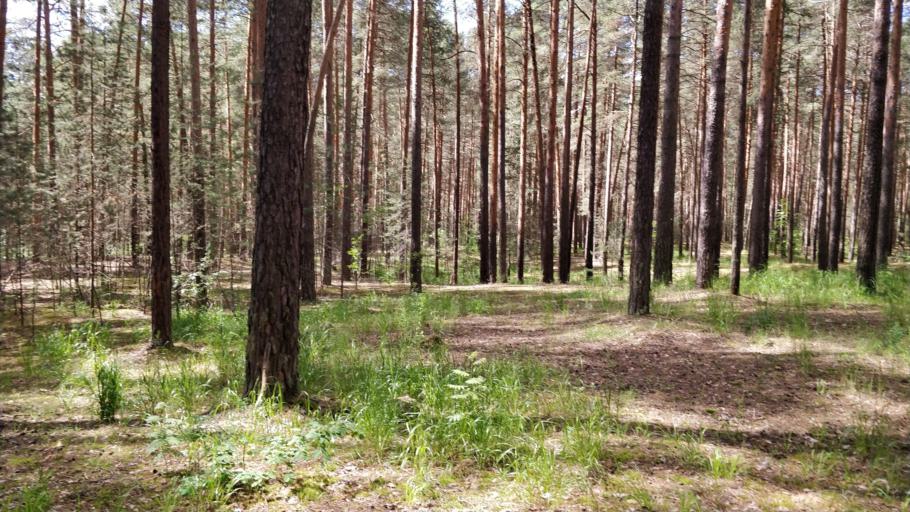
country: RU
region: Perm
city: Perm
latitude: 58.0647
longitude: 56.3005
